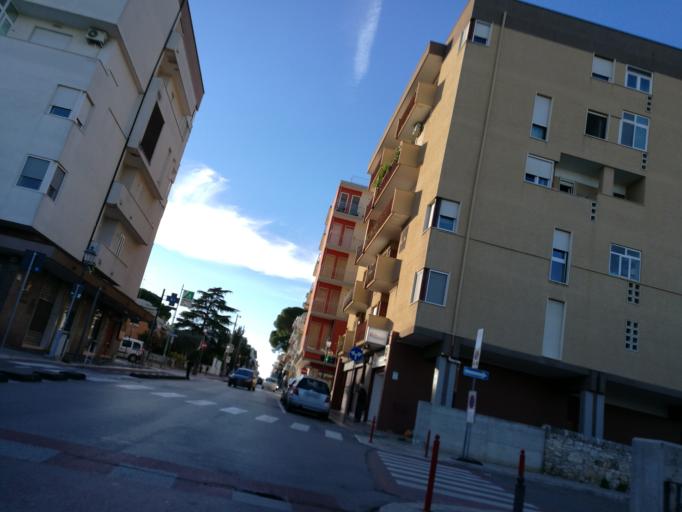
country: IT
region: Apulia
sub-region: Provincia di Bari
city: Adelfia
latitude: 41.0038
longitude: 16.8723
